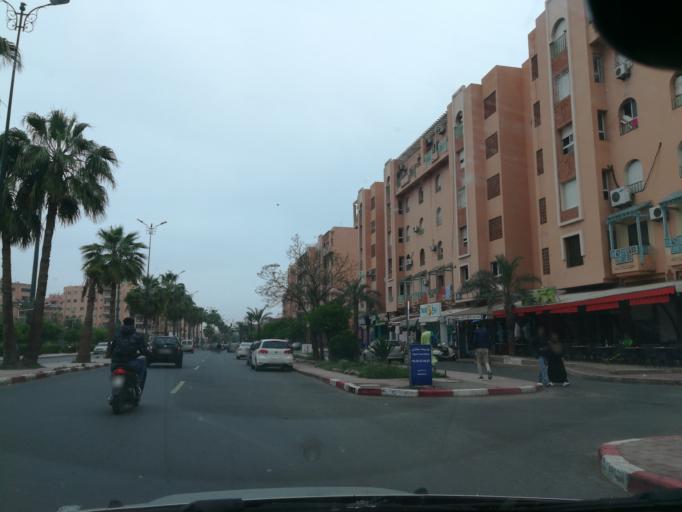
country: MA
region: Marrakech-Tensift-Al Haouz
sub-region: Marrakech
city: Marrakesh
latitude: 31.6631
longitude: -8.0084
